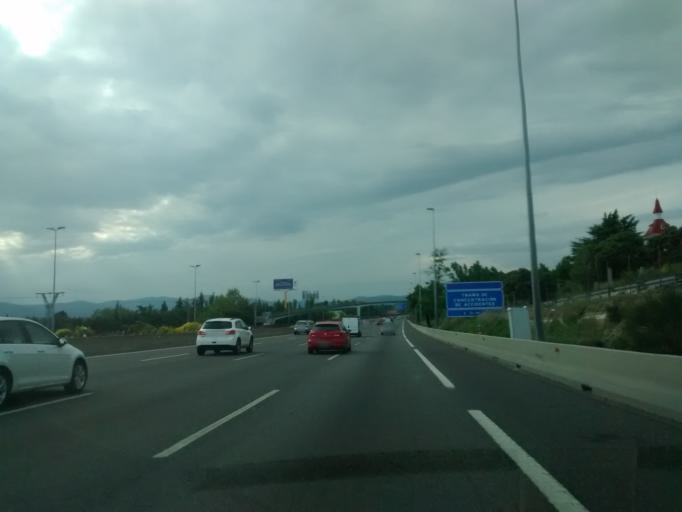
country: ES
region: Madrid
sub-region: Provincia de Madrid
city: Torrelodones
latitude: 40.5820
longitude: -3.9486
